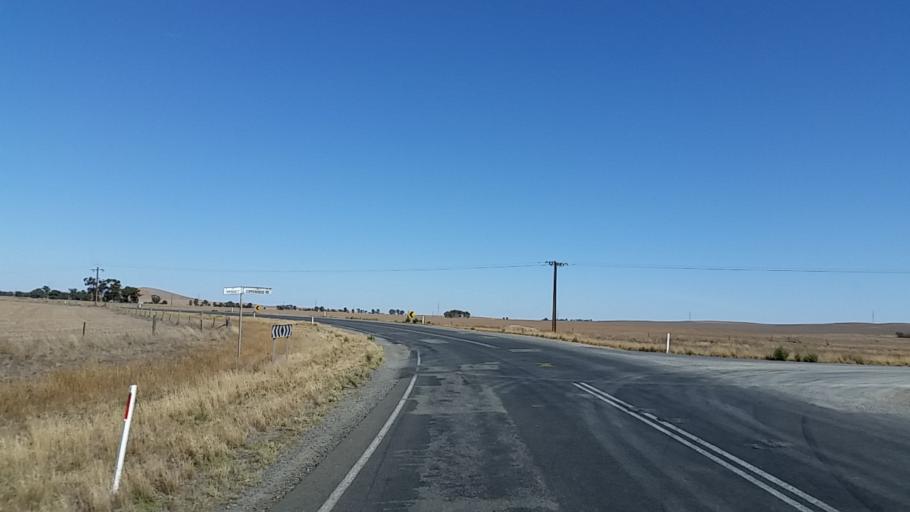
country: AU
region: South Australia
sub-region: Clare and Gilbert Valleys
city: Clare
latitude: -33.6832
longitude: 138.9063
